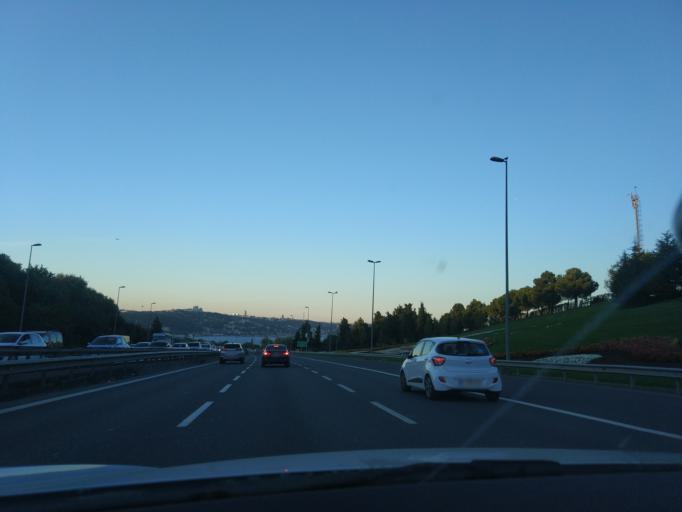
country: TR
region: Istanbul
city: UEskuedar
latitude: 41.0319
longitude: 29.0455
